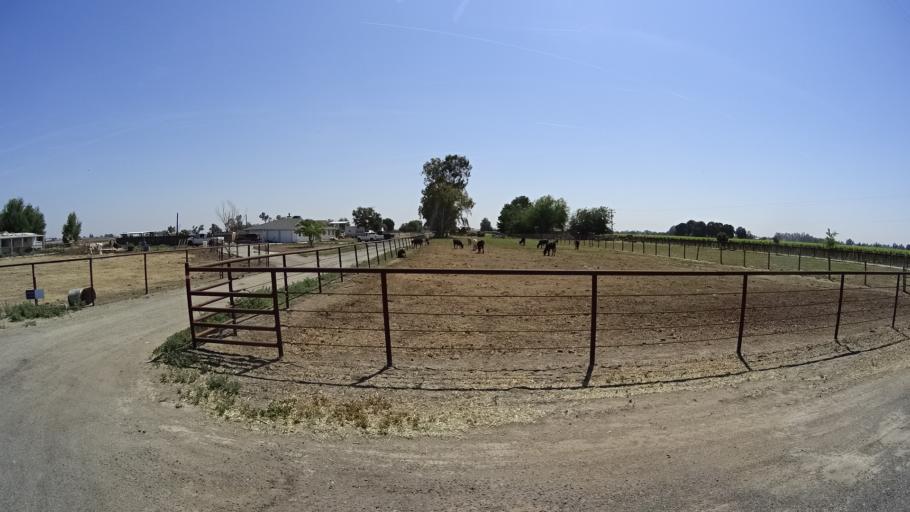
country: US
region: California
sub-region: Fresno County
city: Riverdale
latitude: 36.3717
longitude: -119.8514
